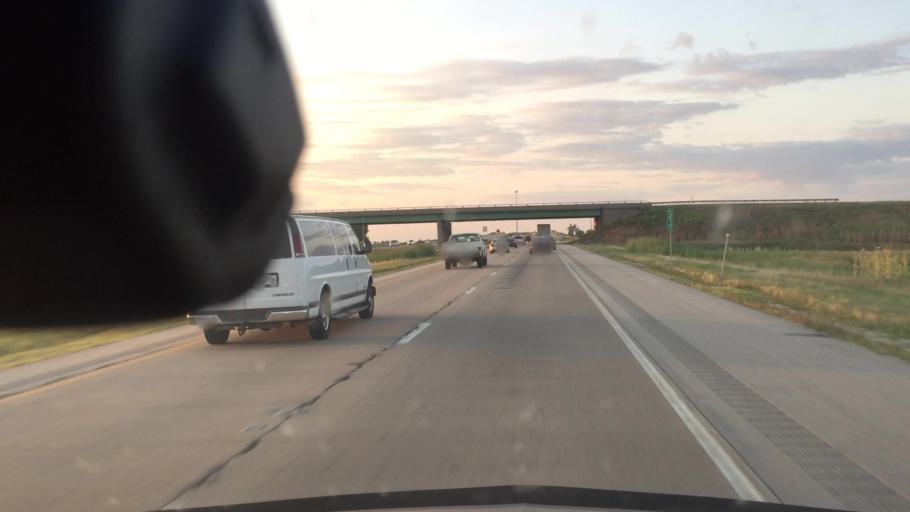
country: US
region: Illinois
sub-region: Livingston County
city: Dwight
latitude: 41.0922
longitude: -88.4506
